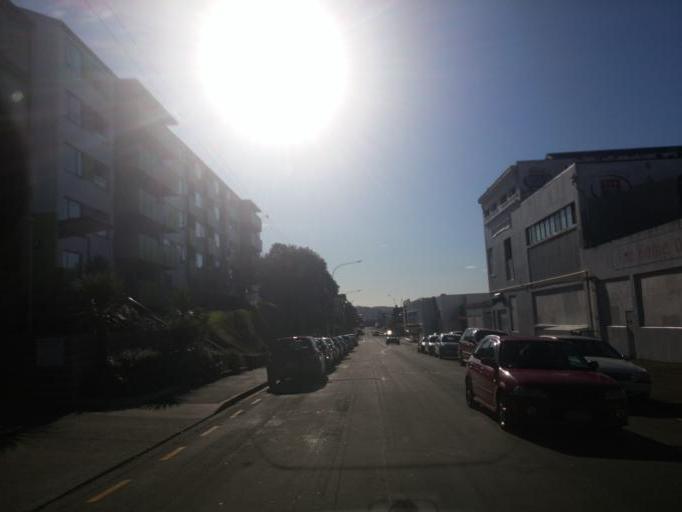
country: NZ
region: Wellington
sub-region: Wellington City
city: Wellington
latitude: -41.3084
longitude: 174.7764
